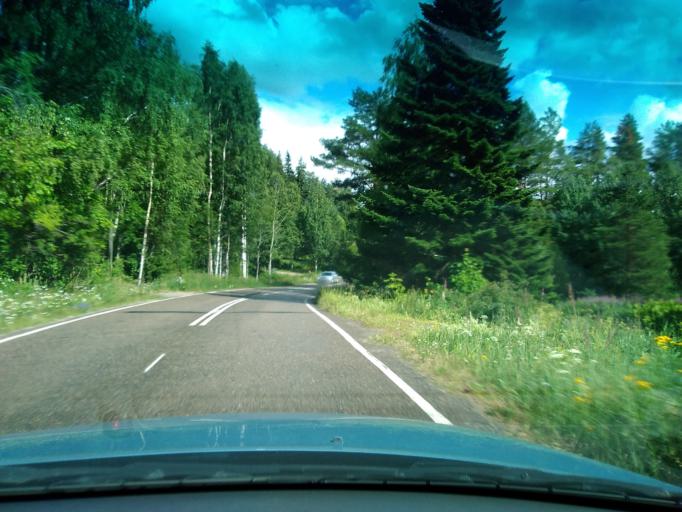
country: FI
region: Central Finland
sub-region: Saarijaervi-Viitasaari
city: Saarijaervi
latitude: 62.7348
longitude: 25.1380
